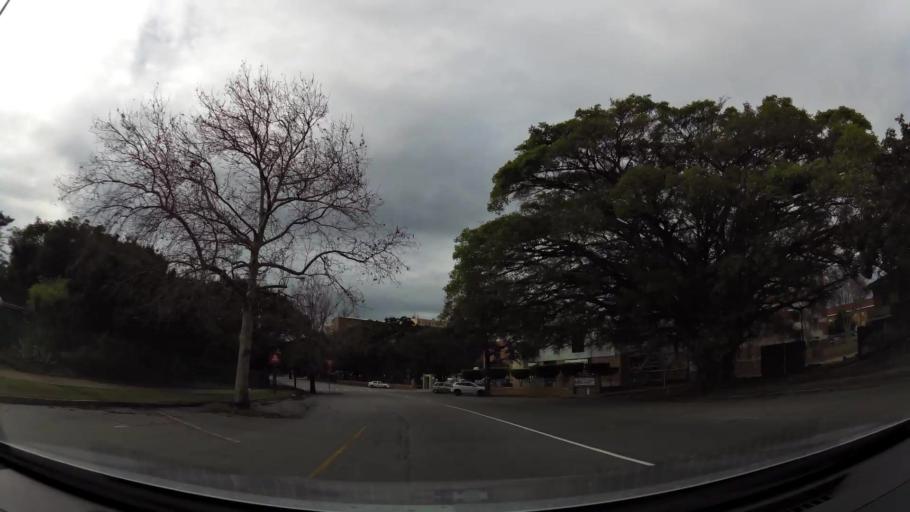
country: ZA
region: Eastern Cape
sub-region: Nelson Mandela Bay Metropolitan Municipality
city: Port Elizabeth
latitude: -33.9673
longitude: 25.6040
